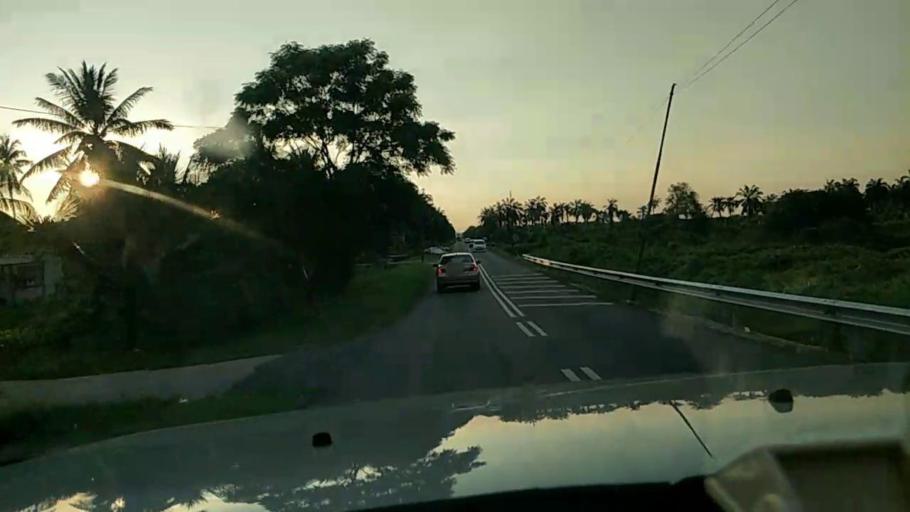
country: MY
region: Selangor
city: Kuala Selangor
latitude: 3.3160
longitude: 101.2818
